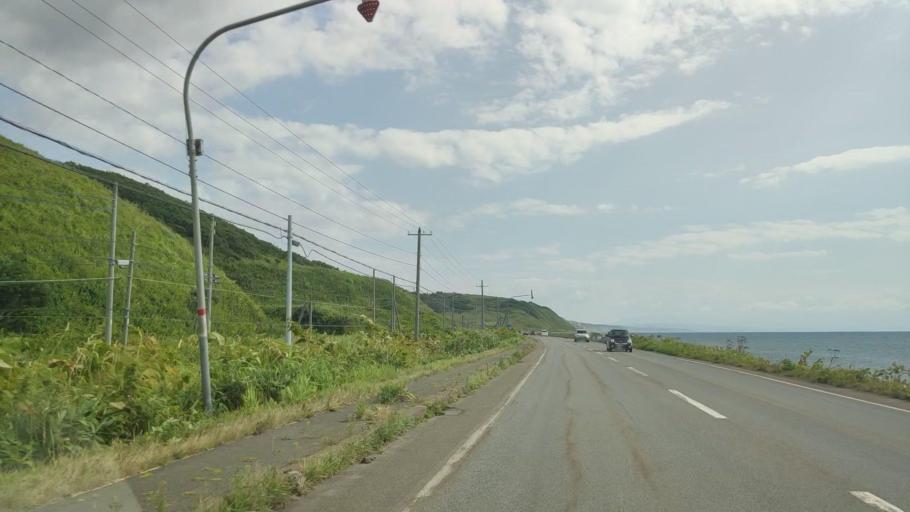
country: JP
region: Hokkaido
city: Rumoi
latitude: 44.1072
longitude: 141.6594
